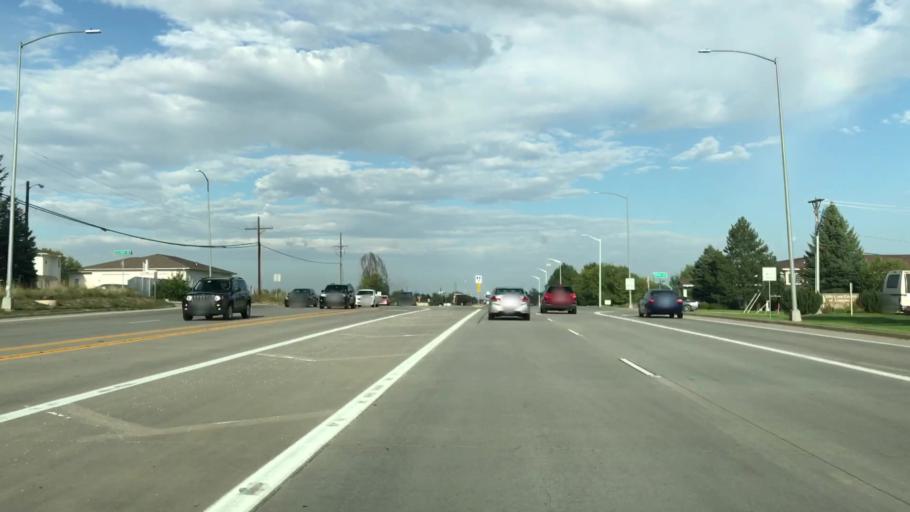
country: US
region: Colorado
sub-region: Boulder County
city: Longmont
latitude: 40.2032
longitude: -105.1073
